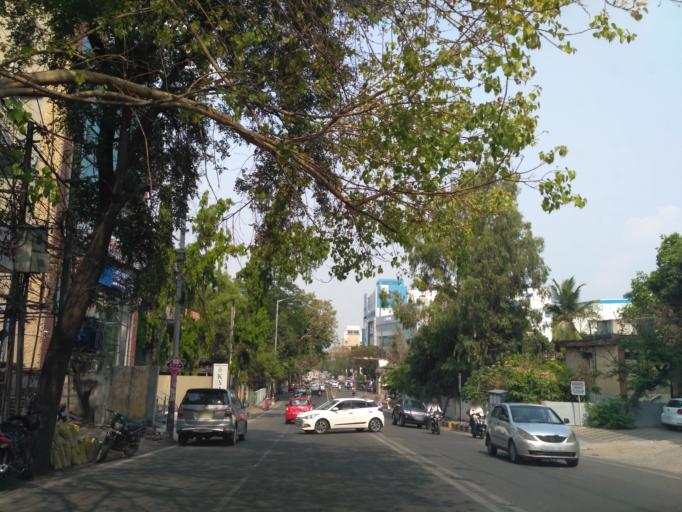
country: IN
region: Telangana
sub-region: Hyderabad
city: Hyderabad
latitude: 17.4172
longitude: 78.4521
